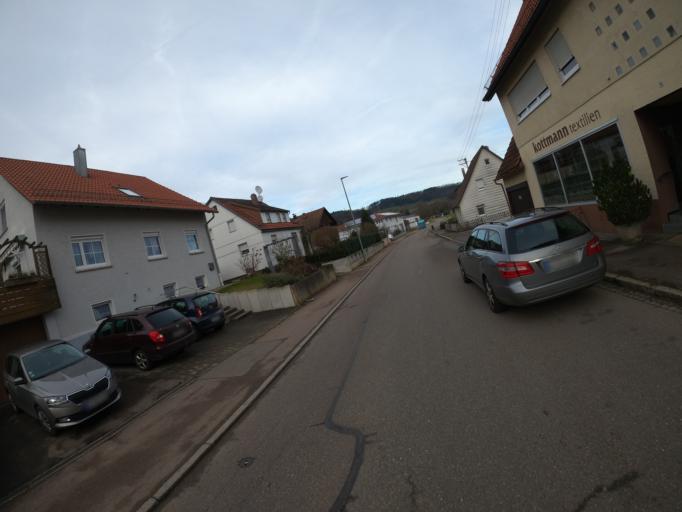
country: DE
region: Baden-Wuerttemberg
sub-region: Regierungsbezirk Stuttgart
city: Ottenbach
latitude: 48.7379
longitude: 9.7494
